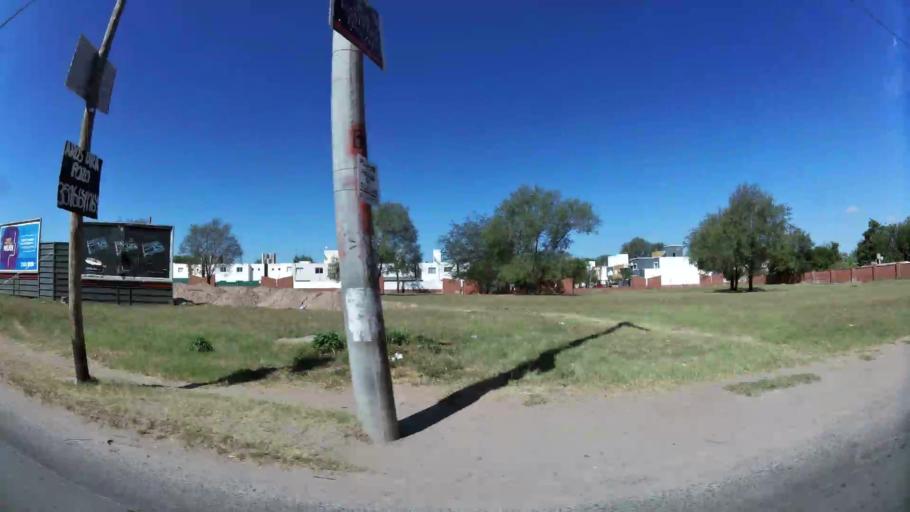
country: AR
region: Cordoba
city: Saldan
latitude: -31.3232
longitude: -64.2885
